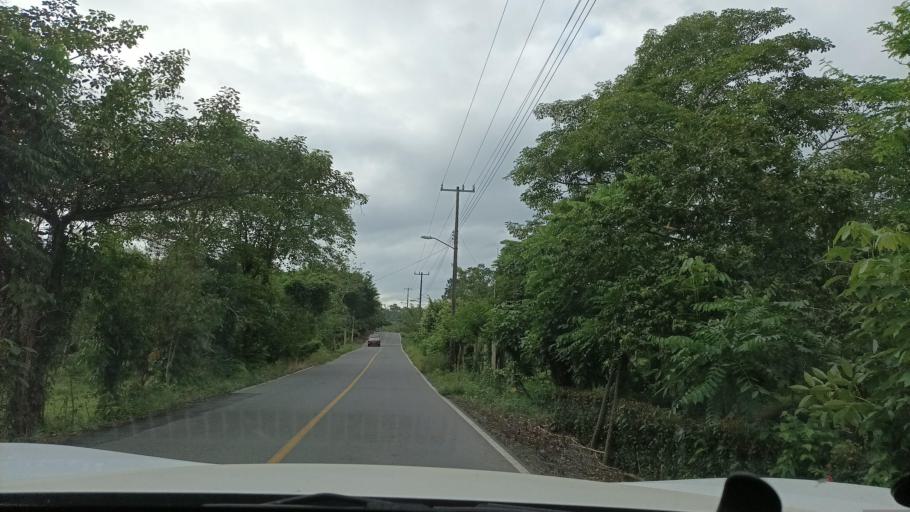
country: MX
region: Veracruz
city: Hidalgotitlan
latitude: 17.7234
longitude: -94.4819
